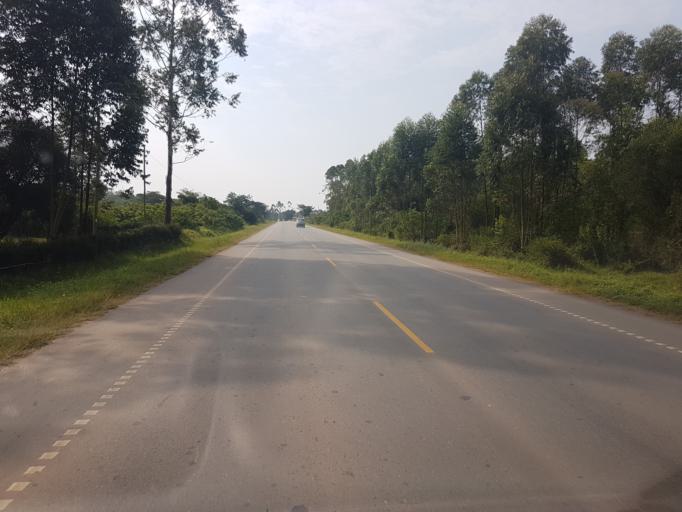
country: UG
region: Western Region
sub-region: Mbarara District
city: Bwizibwera
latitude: -0.6415
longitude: 30.5569
